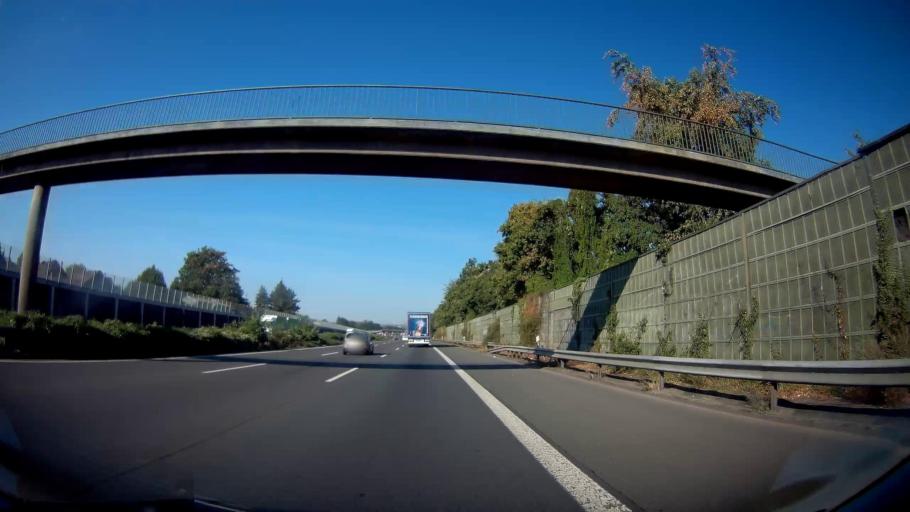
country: DE
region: North Rhine-Westphalia
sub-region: Regierungsbezirk Munster
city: Recklinghausen
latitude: 51.5907
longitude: 7.2300
